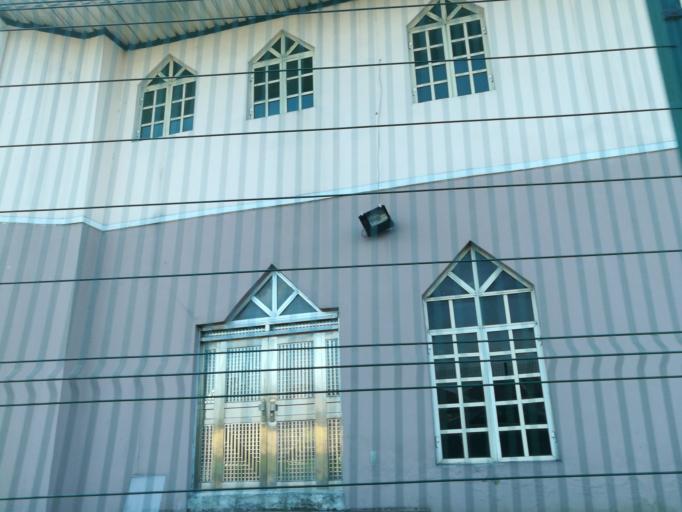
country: NG
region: Rivers
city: Port Harcourt
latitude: 4.8200
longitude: 7.0204
